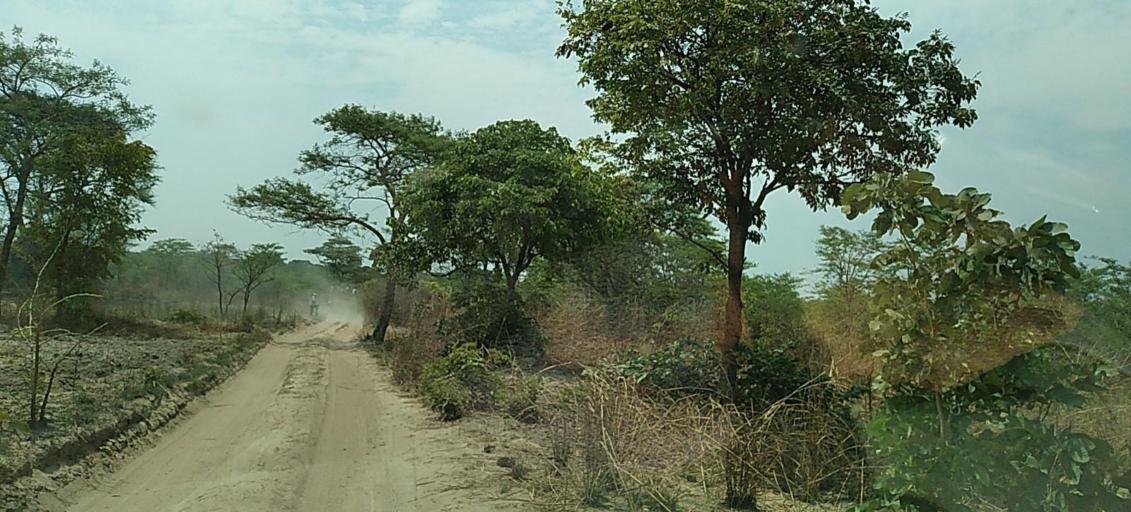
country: ZM
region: Copperbelt
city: Kalulushi
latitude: -12.9277
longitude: 28.1060
